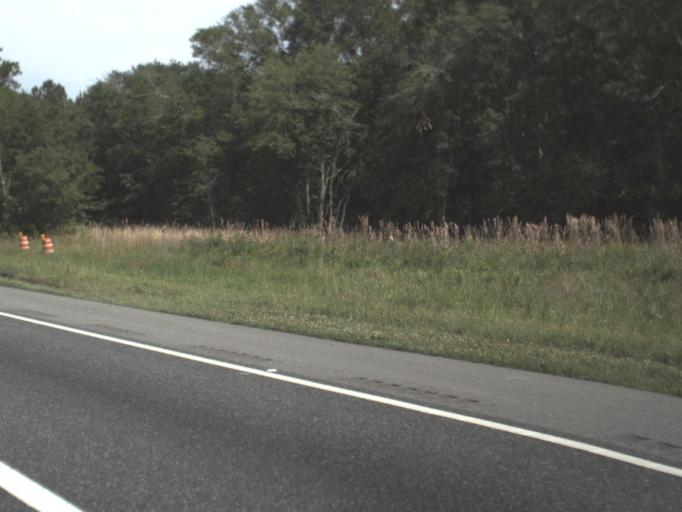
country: US
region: Florida
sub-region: Columbia County
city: Five Points
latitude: 30.2451
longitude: -82.6689
